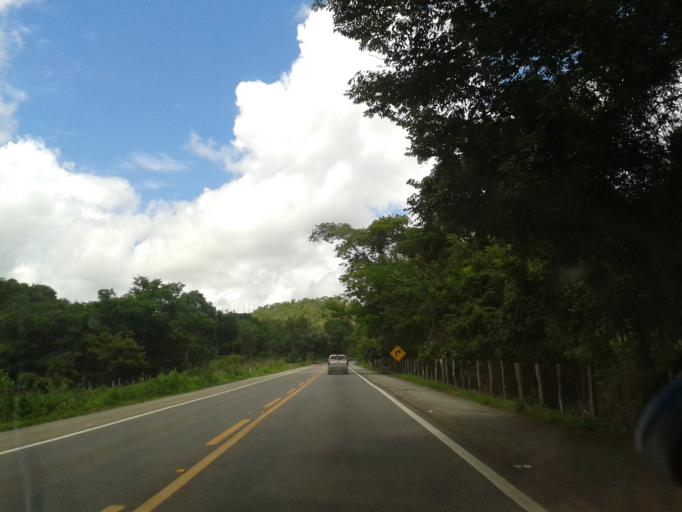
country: BR
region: Goias
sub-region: Goias
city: Goias
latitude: -15.8814
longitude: -50.1035
